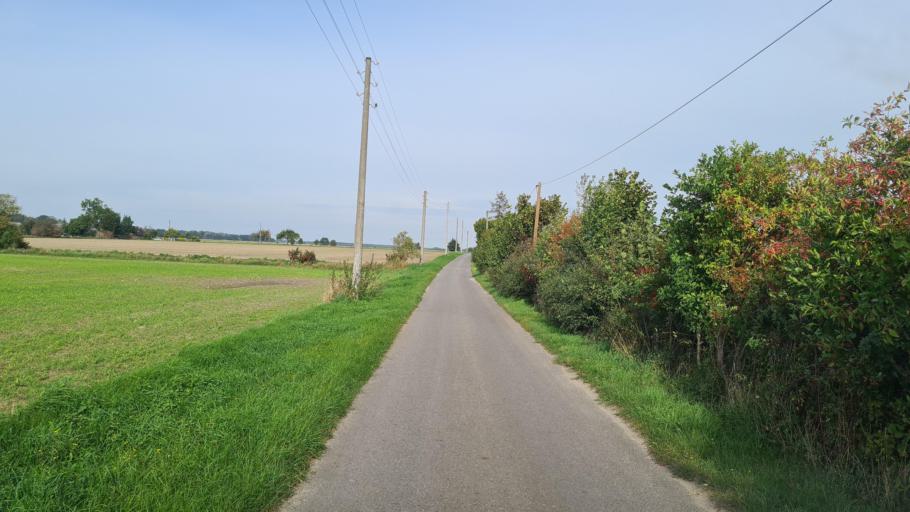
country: DE
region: Brandenburg
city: Sonnewalde
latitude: 51.7165
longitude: 13.6257
